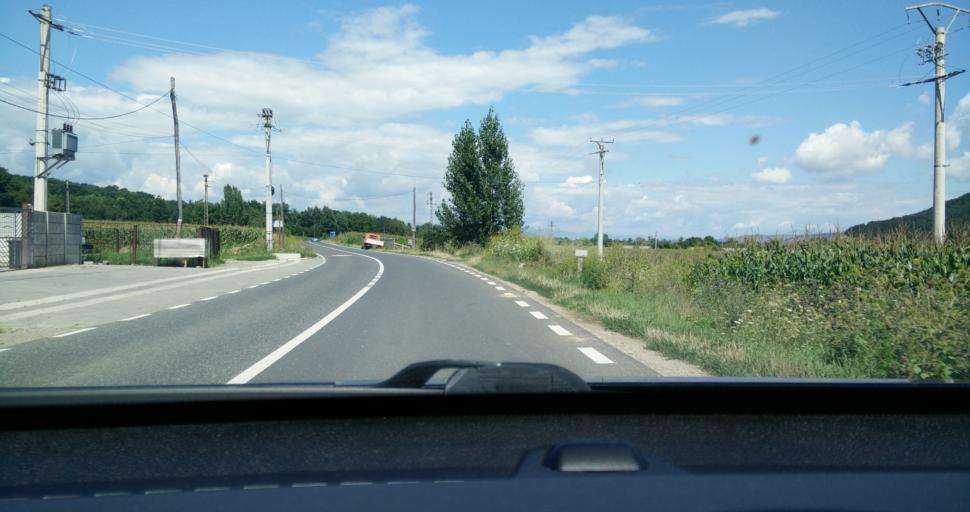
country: RO
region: Alba
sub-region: Comuna Sasciori
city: Sebesel
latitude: 45.8931
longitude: 23.5611
